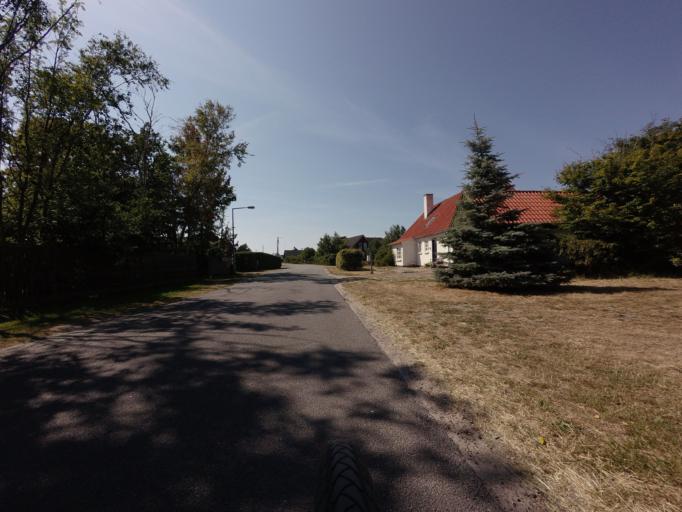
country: DK
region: North Denmark
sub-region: Laeso Kommune
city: Byrum
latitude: 57.2954
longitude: 10.9315
